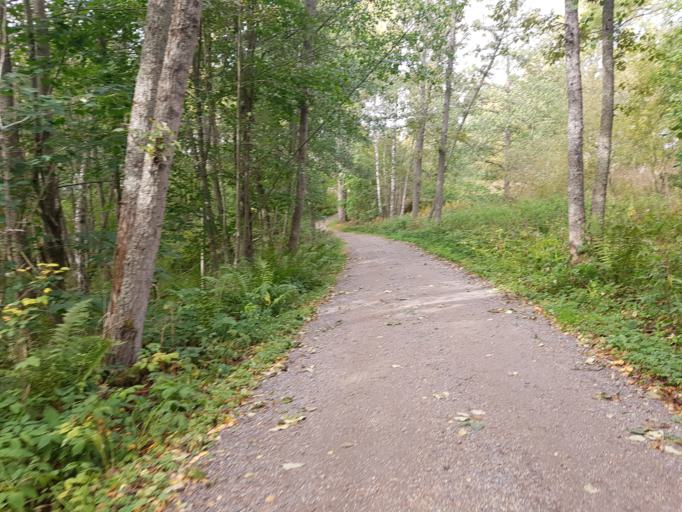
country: FI
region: Uusimaa
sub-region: Helsinki
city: Helsinki
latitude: 60.1384
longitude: 24.9989
